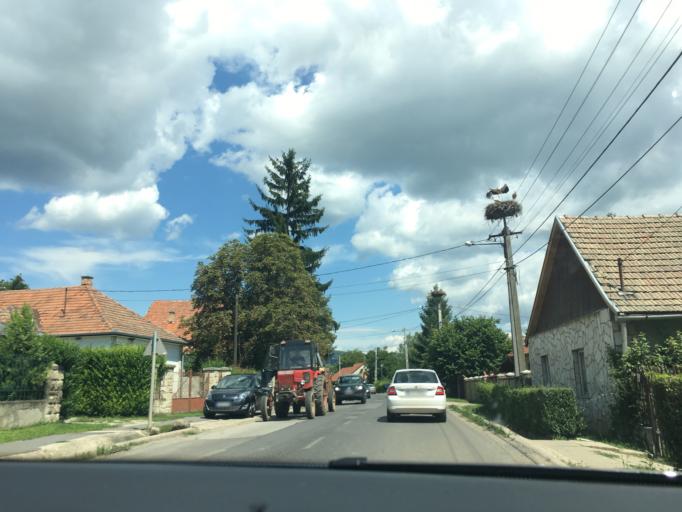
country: HU
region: Borsod-Abauj-Zemplen
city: Tarcal
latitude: 48.1661
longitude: 21.3662
